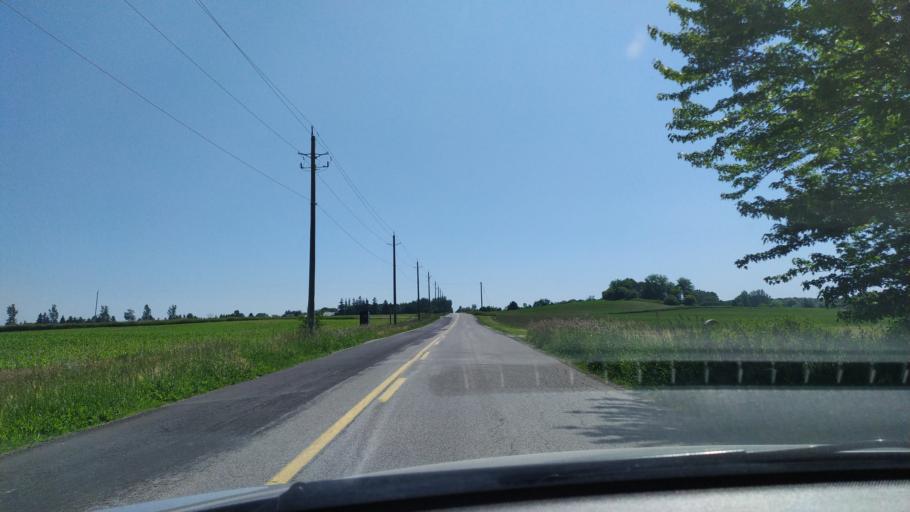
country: CA
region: Ontario
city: Waterloo
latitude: 43.4601
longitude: -80.7091
